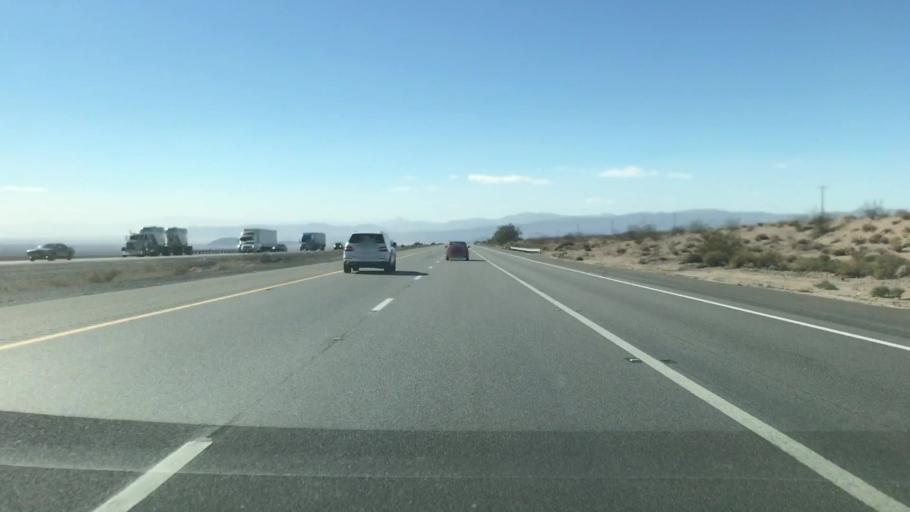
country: US
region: Nevada
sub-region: Clark County
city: Sandy Valley
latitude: 35.3574
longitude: -115.9298
